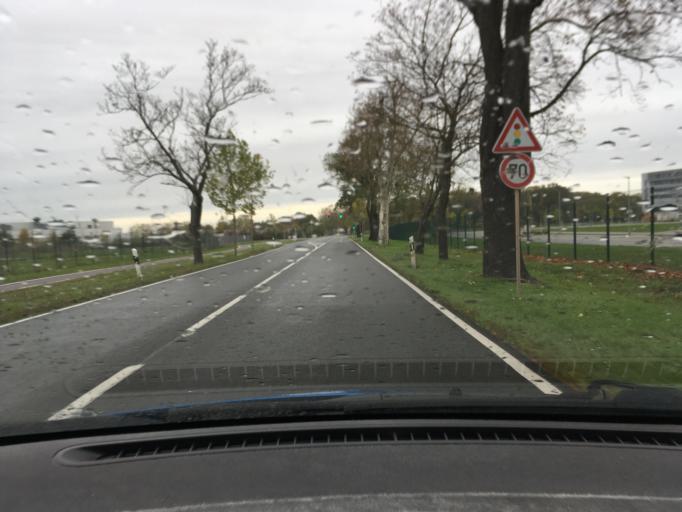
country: DE
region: Saxony-Anhalt
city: Rodleben
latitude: 51.9024
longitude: 12.2128
